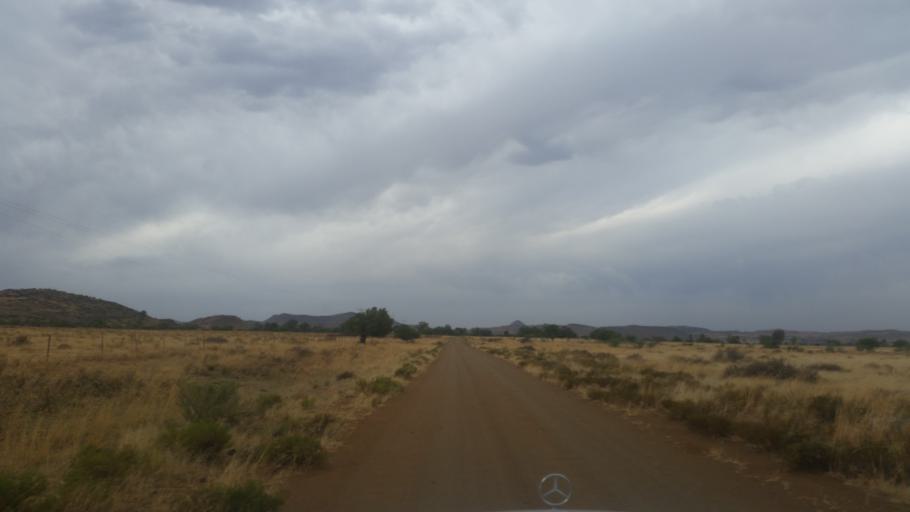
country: ZA
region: Orange Free State
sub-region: Xhariep District Municipality
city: Trompsburg
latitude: -30.5023
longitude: 25.9521
